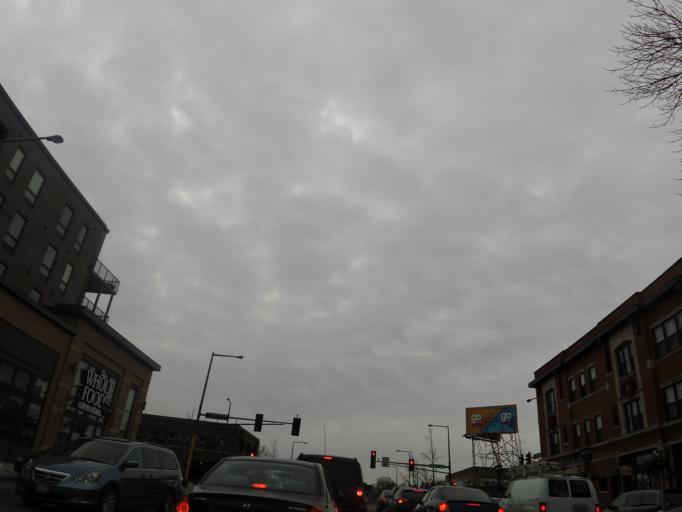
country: US
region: Minnesota
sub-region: Ramsey County
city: Falcon Heights
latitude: 44.9470
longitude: -93.1671
